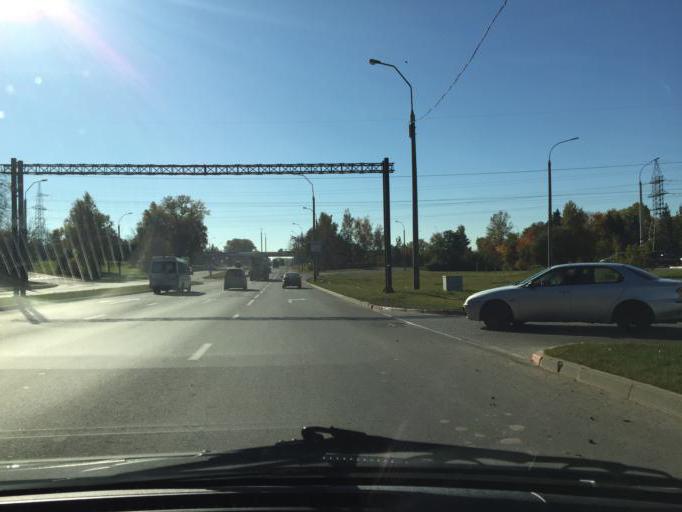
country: BY
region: Minsk
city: Syenitsa
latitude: 53.8387
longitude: 27.5331
